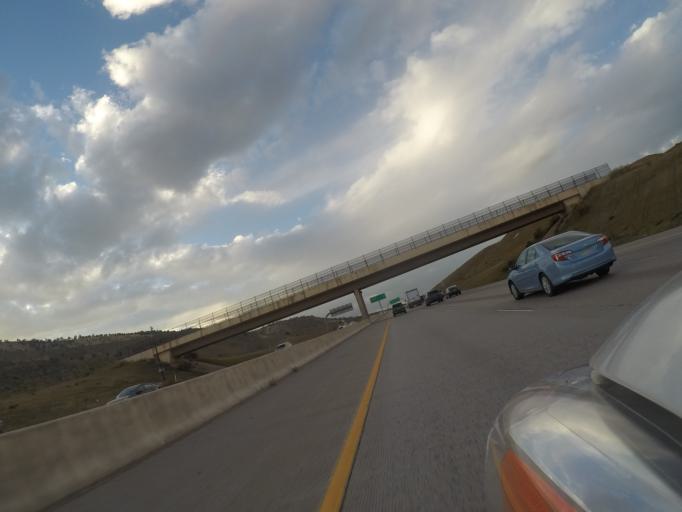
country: US
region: Colorado
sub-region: Jefferson County
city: West Pleasant View
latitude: 39.6950
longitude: -105.1900
